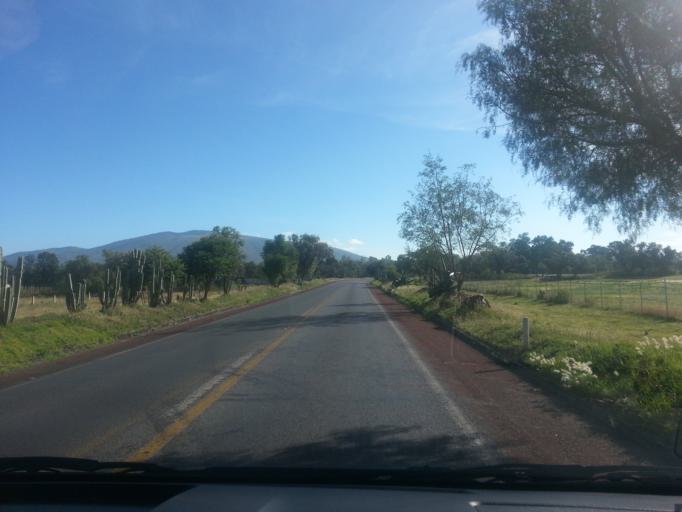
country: MX
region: Morelos
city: Teotihuacan de Arista
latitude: 19.6827
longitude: -98.8571
